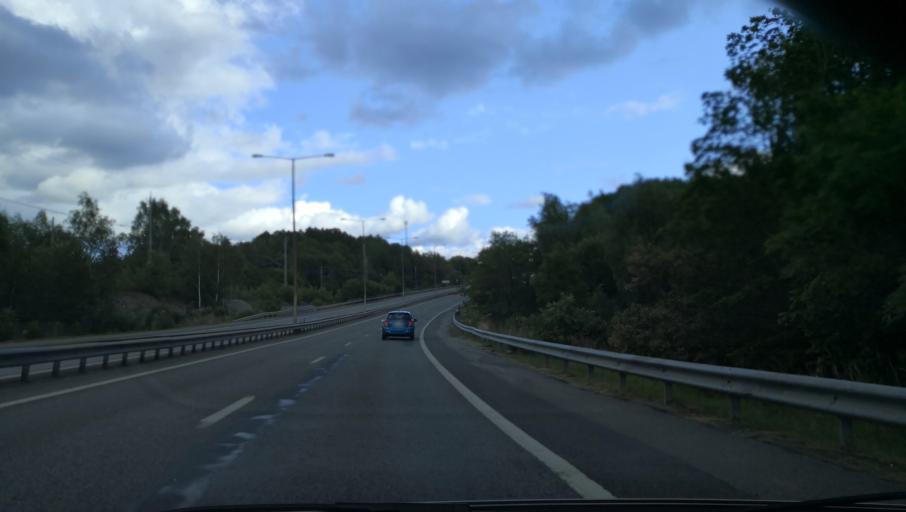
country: SE
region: Stockholm
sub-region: Haninge Kommun
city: Handen
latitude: 59.2353
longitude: 18.1163
